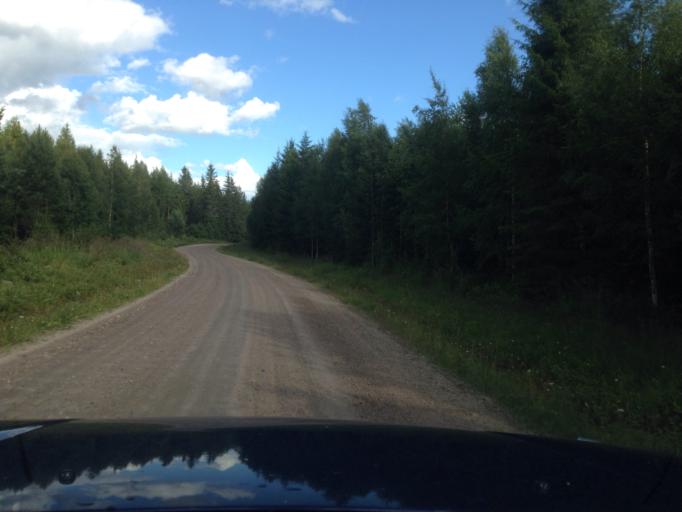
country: SE
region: Dalarna
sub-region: Ludvika Kommun
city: Abborrberget
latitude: 60.3082
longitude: 14.6029
